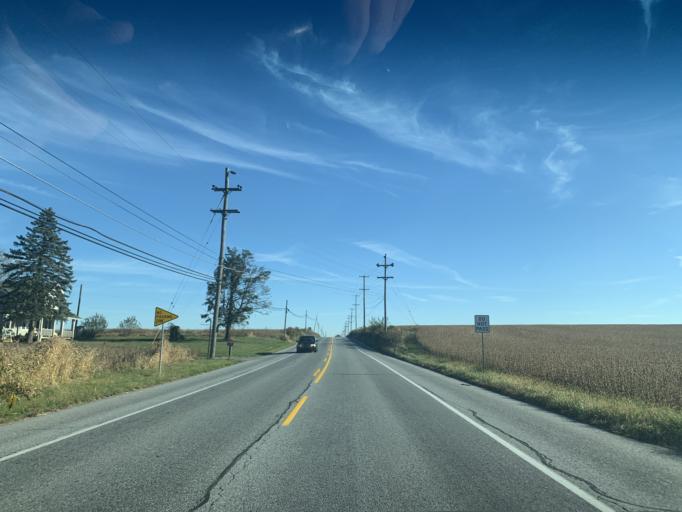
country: US
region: Pennsylvania
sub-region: Chester County
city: Oxford
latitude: 39.8259
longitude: -75.9585
